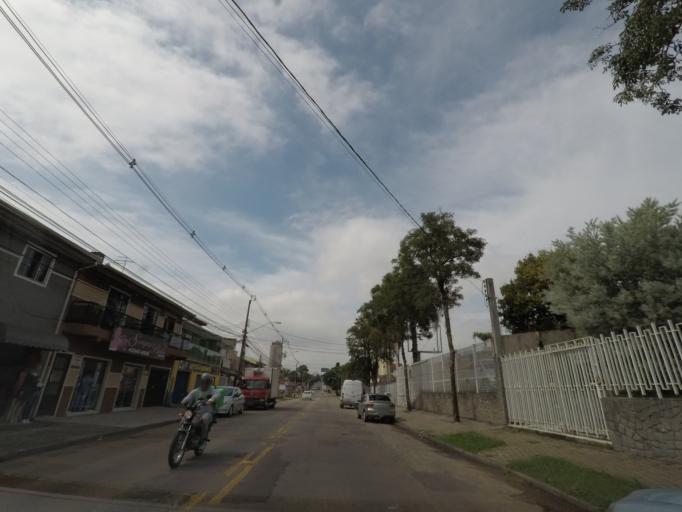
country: BR
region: Parana
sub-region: Curitiba
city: Curitiba
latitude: -25.4891
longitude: -49.3008
